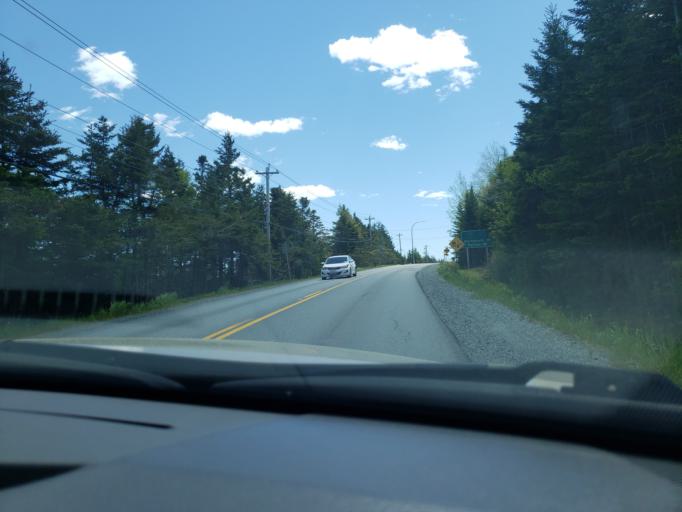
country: CA
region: Nova Scotia
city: Cole Harbour
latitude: 44.7276
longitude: -63.3066
